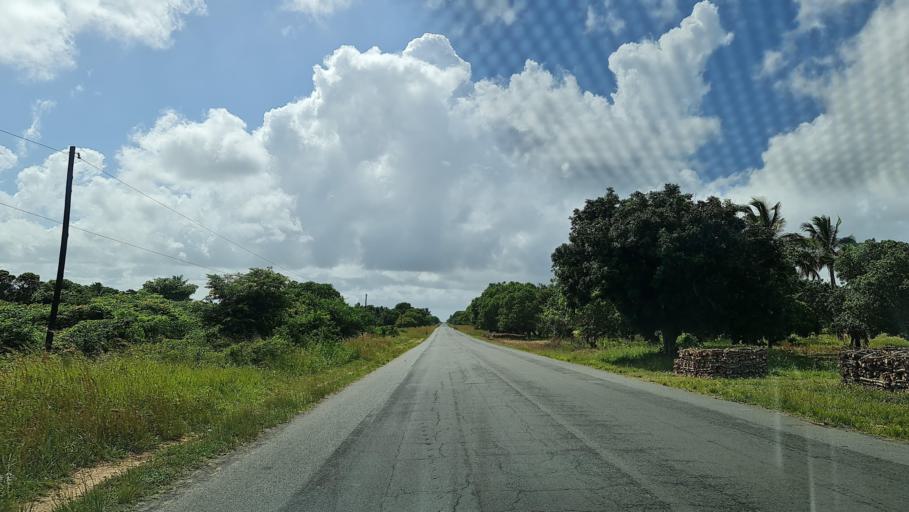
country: MZ
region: Gaza
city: Manjacaze
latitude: -24.6770
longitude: 34.5899
